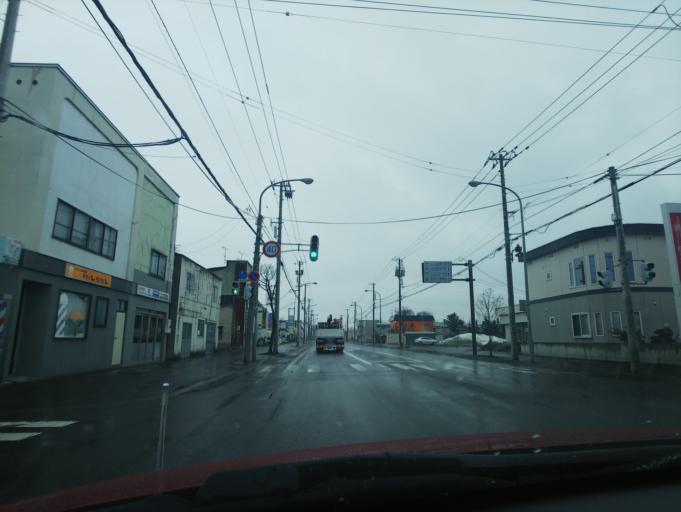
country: JP
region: Hokkaido
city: Nayoro
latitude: 44.1832
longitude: 142.3900
